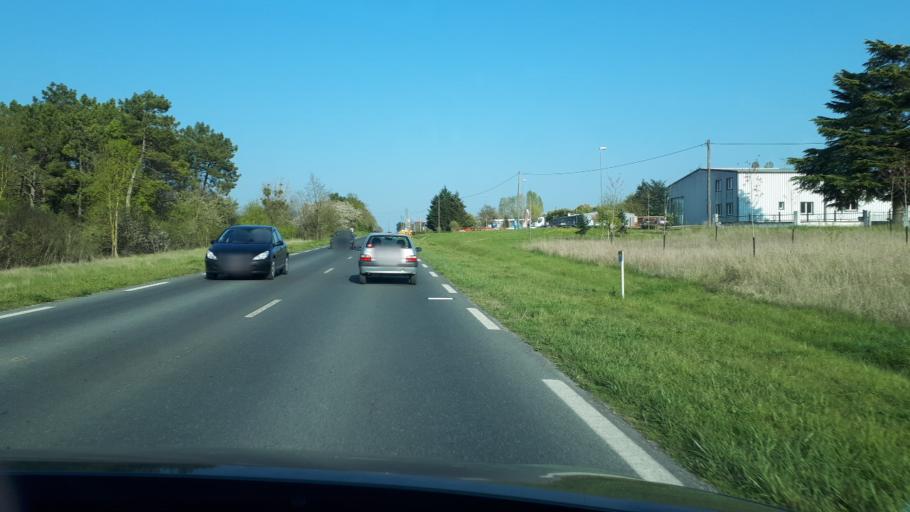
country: FR
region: Centre
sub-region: Departement du Loir-et-Cher
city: Saint-Georges-sur-Cher
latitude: 47.3299
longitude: 1.1461
